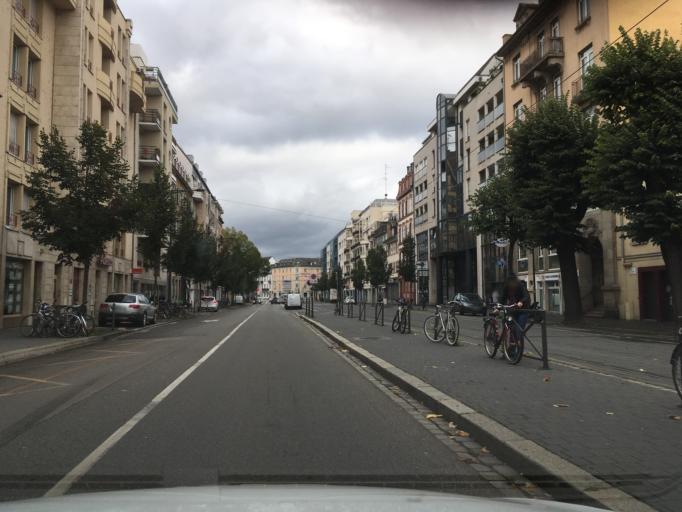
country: FR
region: Alsace
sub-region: Departement du Bas-Rhin
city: Strasbourg
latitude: 48.5859
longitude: 7.7399
